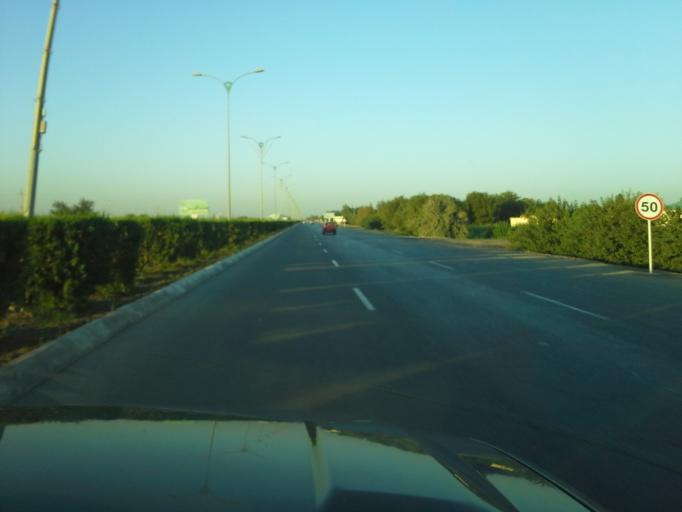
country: TM
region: Dasoguz
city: Dasoguz
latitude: 41.8038
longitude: 59.9017
